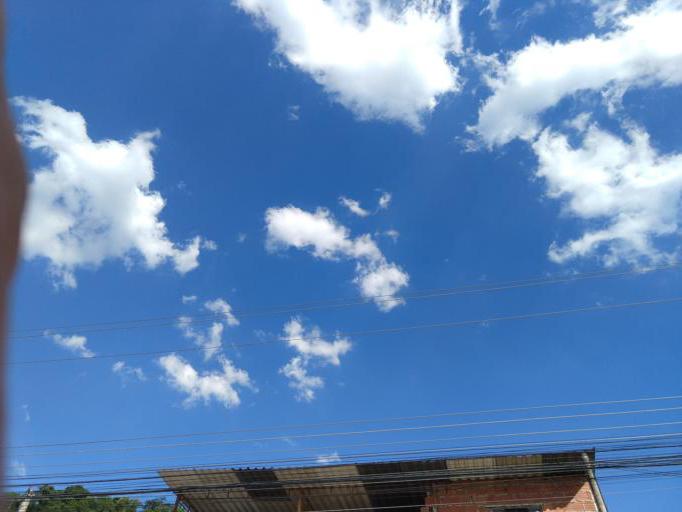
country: BR
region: Rio de Janeiro
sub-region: Barra Mansa
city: Barra Mansa
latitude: -22.5541
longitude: -44.1484
